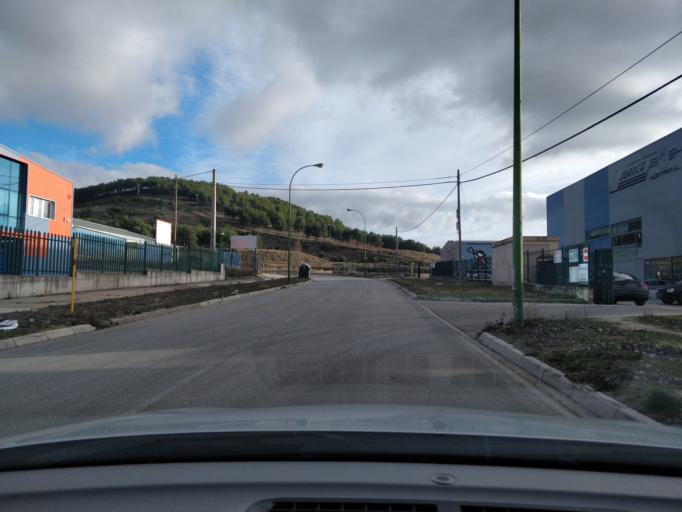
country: ES
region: Castille and Leon
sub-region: Provincia de Burgos
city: Villalbilla de Burgos
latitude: 42.3640
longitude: -3.7519
